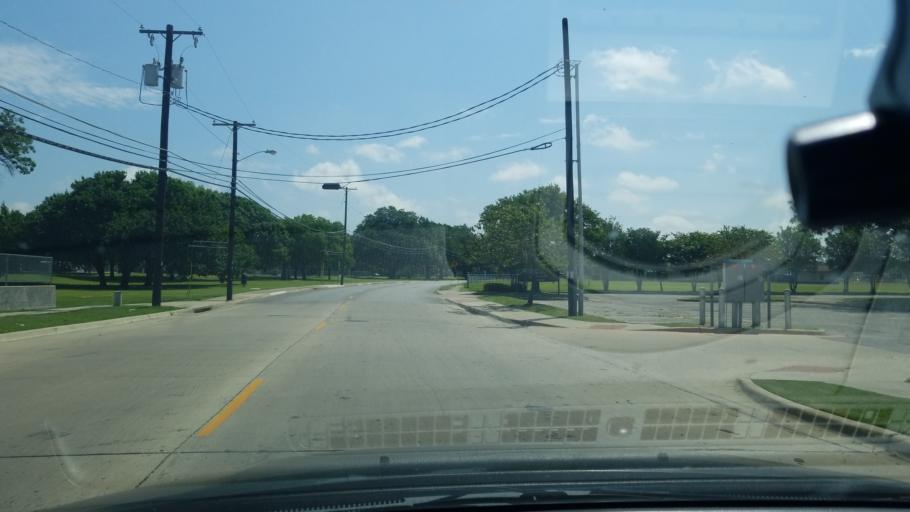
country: US
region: Texas
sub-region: Dallas County
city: Balch Springs
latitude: 32.7424
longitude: -96.6915
